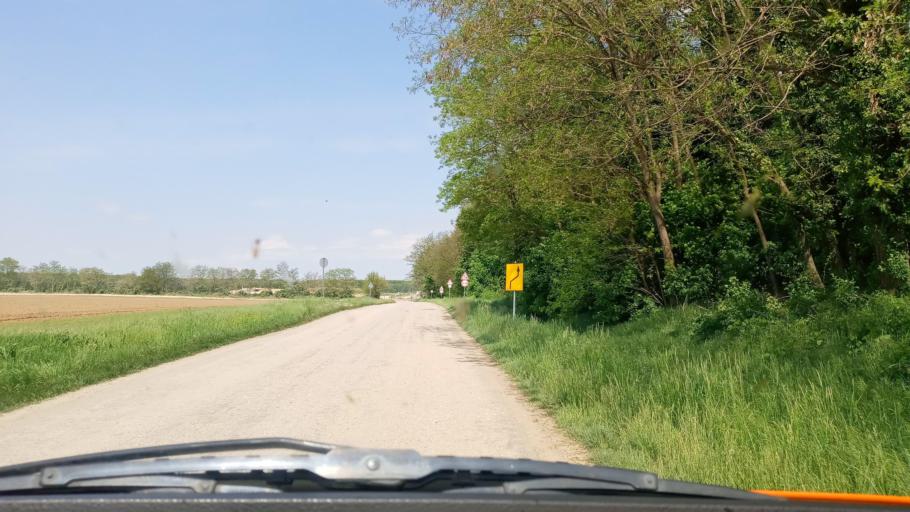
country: HU
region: Baranya
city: Boly
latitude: 45.8847
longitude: 18.5683
